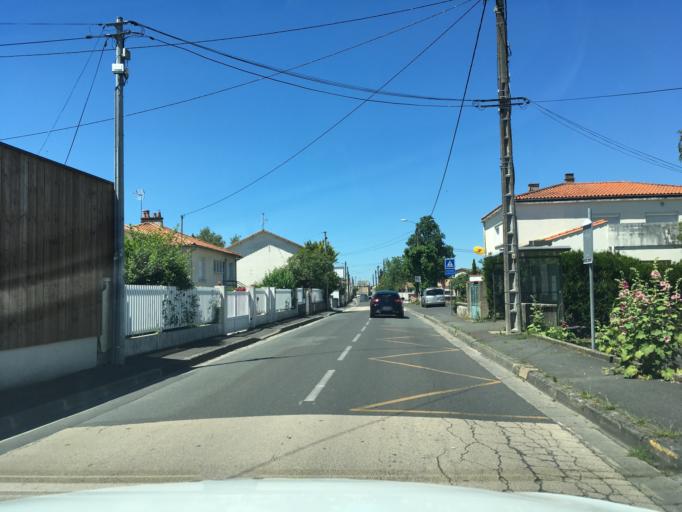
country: FR
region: Poitou-Charentes
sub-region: Departement des Deux-Sevres
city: Niort
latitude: 46.3252
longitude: -0.4285
